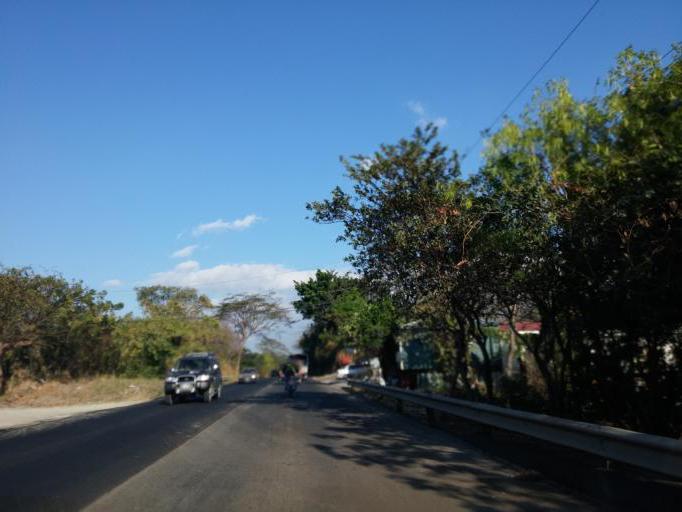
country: CR
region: Heredia
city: Colon
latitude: 9.9336
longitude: -84.2362
